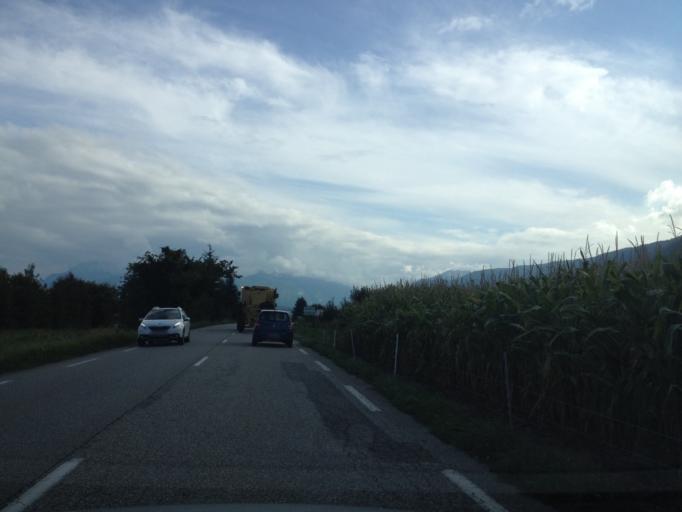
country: FR
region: Rhone-Alpes
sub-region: Departement de la Savoie
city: Le Bourget-du-Lac
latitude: 45.6314
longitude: 5.8626
